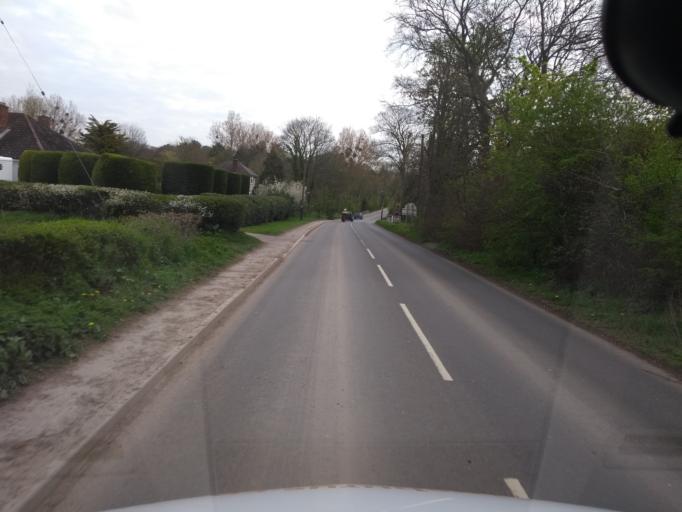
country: GB
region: England
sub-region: Somerset
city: Langport
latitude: 51.0449
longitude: -2.8151
